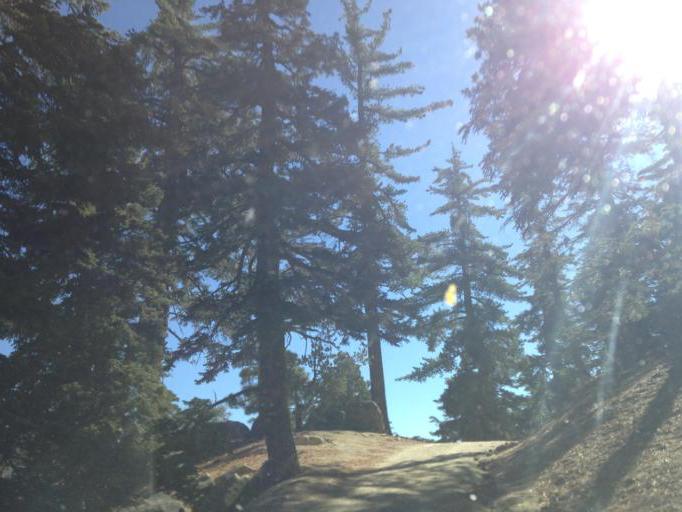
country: US
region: California
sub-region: Riverside County
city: Idyllwild-Pine Cove
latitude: 33.8255
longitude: -116.7559
